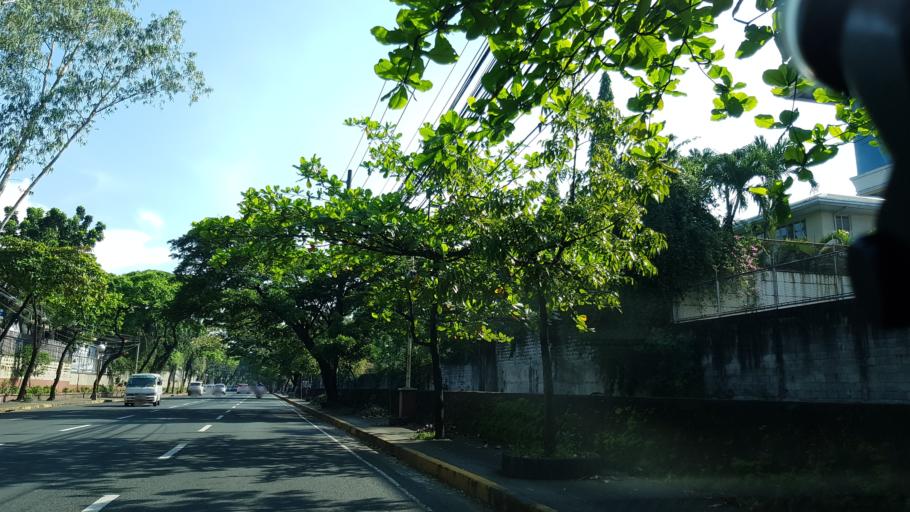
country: PH
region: Metro Manila
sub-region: Pasig
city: Pasig City
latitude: 14.5861
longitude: 121.0710
